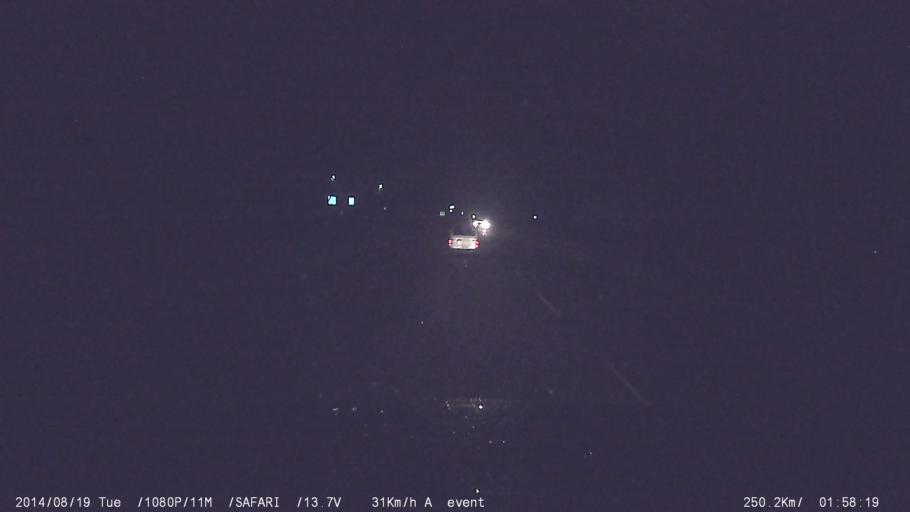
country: IN
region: Tamil Nadu
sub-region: Coimbatore
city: Madukkarai
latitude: 10.8641
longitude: 76.8760
